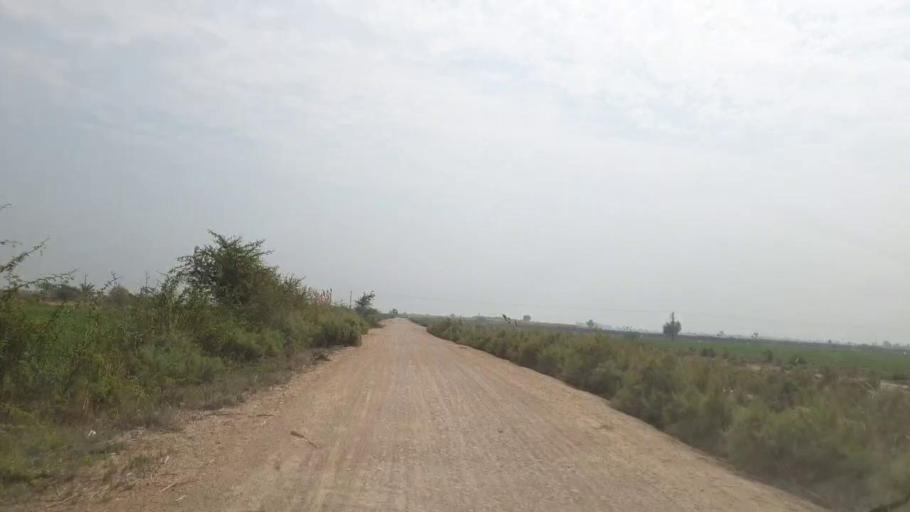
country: PK
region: Sindh
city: Mirpur Khas
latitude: 25.5430
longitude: 69.1269
